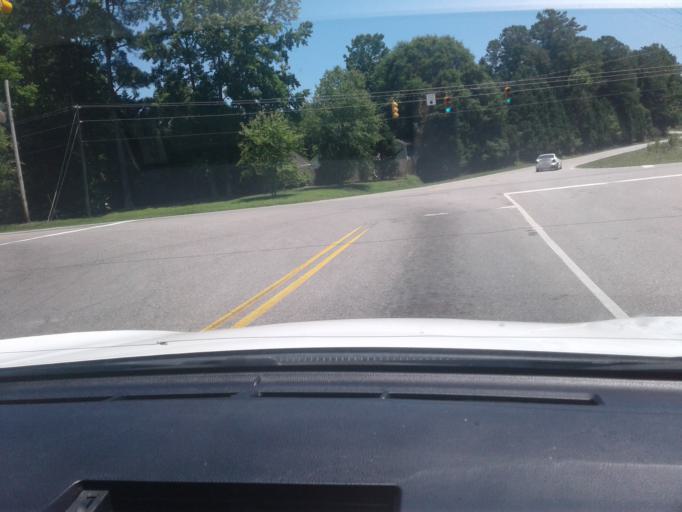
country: US
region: North Carolina
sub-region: Harnett County
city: Erwin
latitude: 35.3113
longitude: -78.6972
